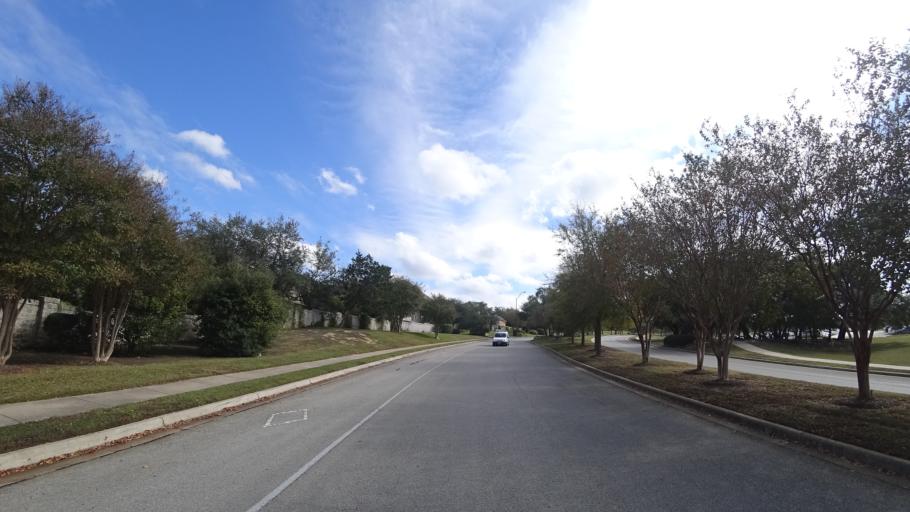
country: US
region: Texas
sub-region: Travis County
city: Hudson Bend
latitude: 30.3670
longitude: -97.9032
